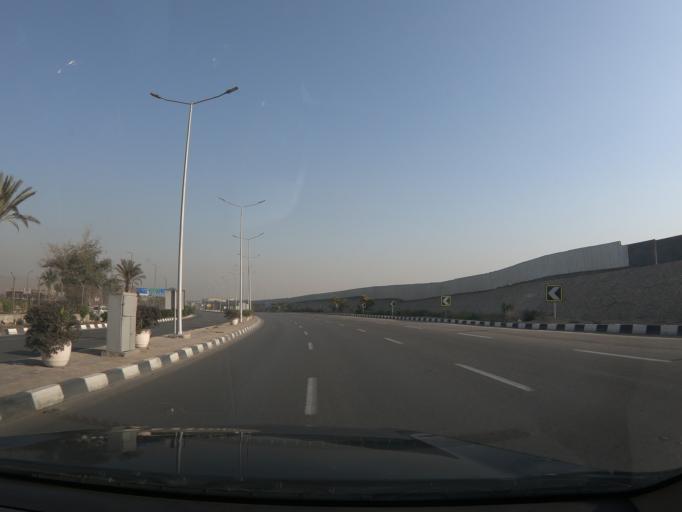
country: EG
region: Muhafazat al Qalyubiyah
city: Al Khankah
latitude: 30.1038
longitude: 31.3879
